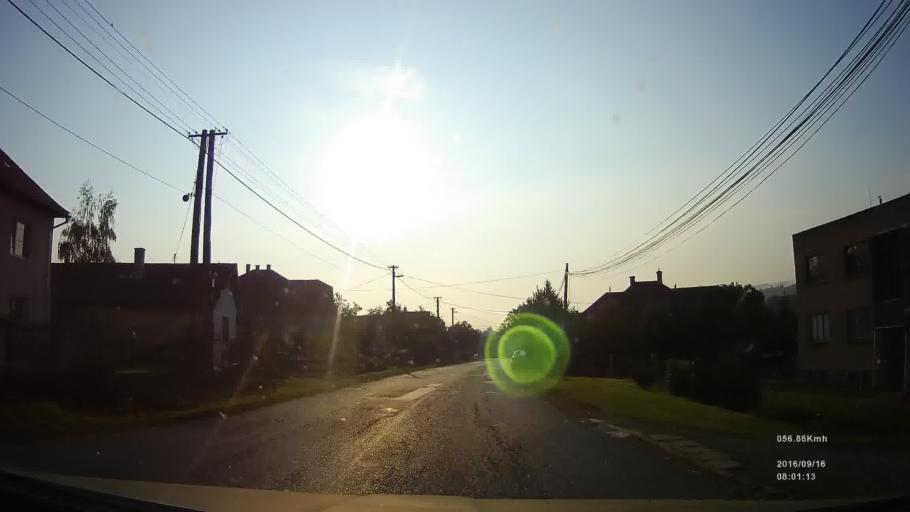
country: SK
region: Presovsky
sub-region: Okres Presov
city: Presov
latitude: 48.9151
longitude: 21.1692
